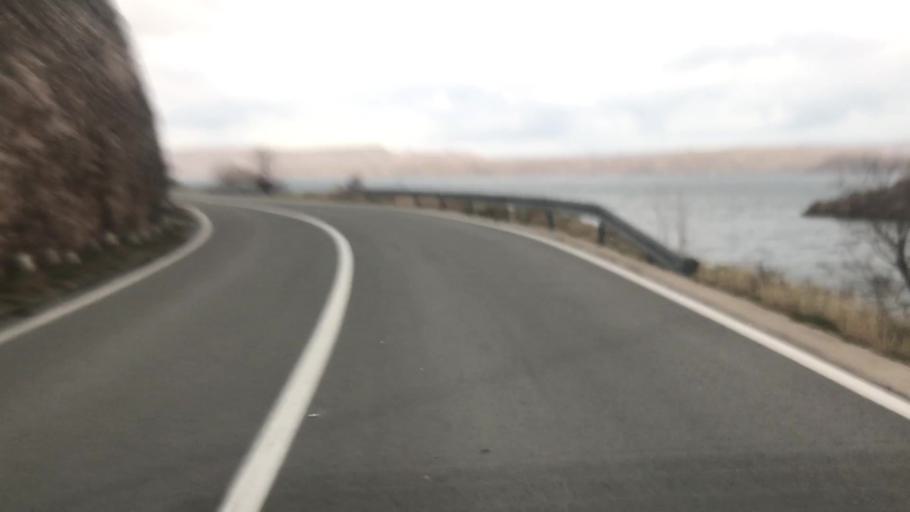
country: HR
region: Licko-Senjska
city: Karlobag
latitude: 44.5177
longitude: 15.0930
